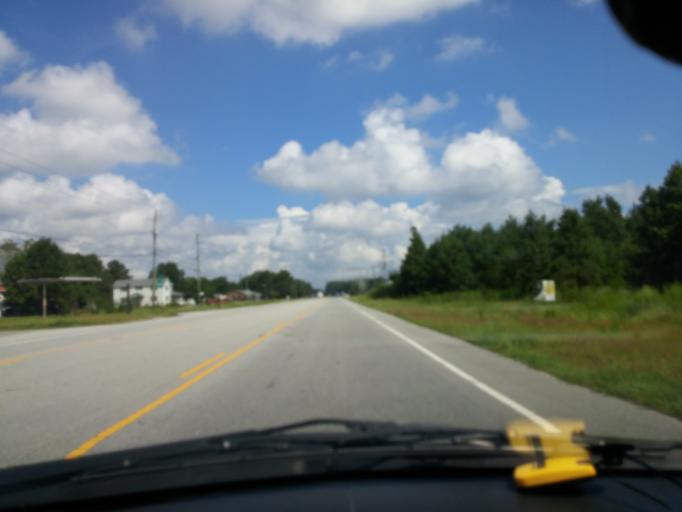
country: US
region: North Carolina
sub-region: Duplin County
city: Beulaville
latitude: 35.0735
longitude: -77.7352
